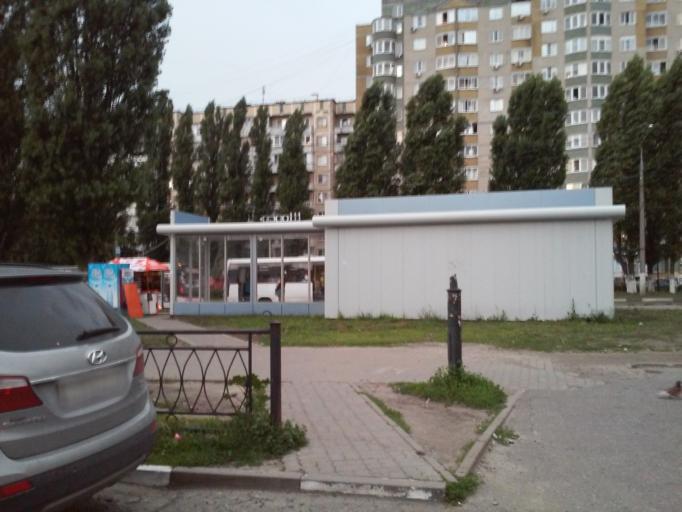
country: RU
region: Belgorod
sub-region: Belgorodskiy Rayon
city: Belgorod
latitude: 50.5679
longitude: 36.5710
